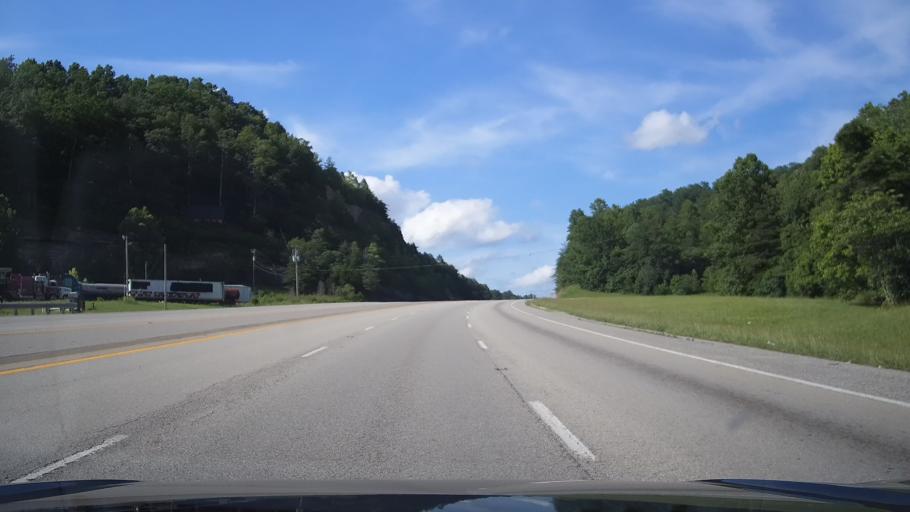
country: US
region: Kentucky
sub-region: Lawrence County
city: Louisa
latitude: 38.0338
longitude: -82.6519
